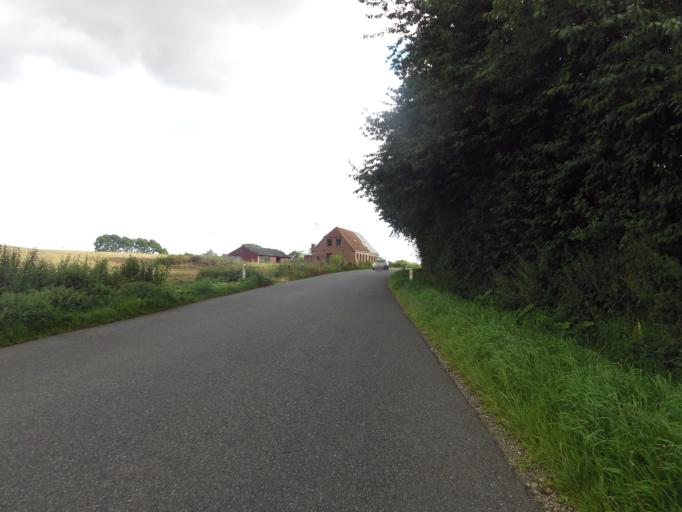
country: DK
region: South Denmark
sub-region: Haderslev Kommune
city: Haderslev
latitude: 55.2372
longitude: 9.4681
